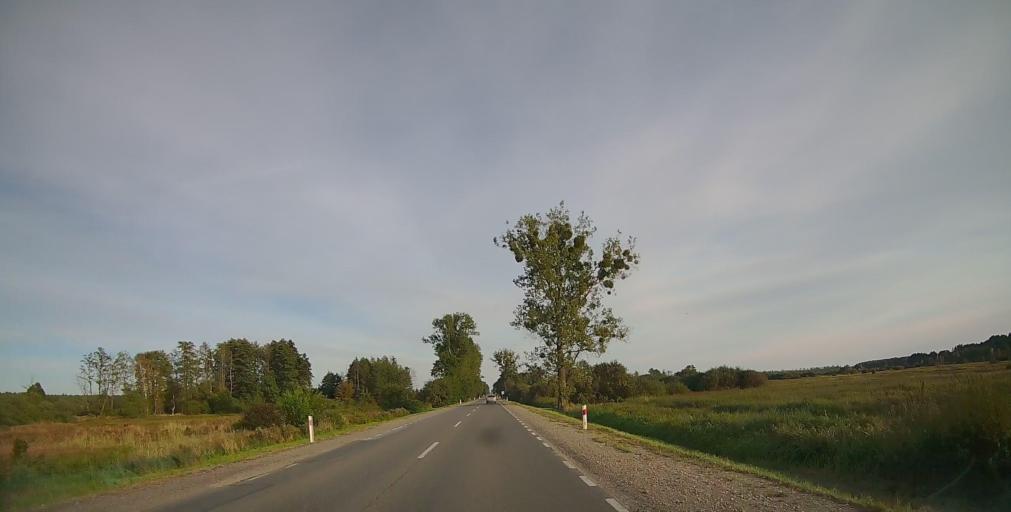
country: PL
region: Masovian Voivodeship
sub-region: Powiat piaseczynski
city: Baniocha
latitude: 52.0344
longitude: 21.1007
